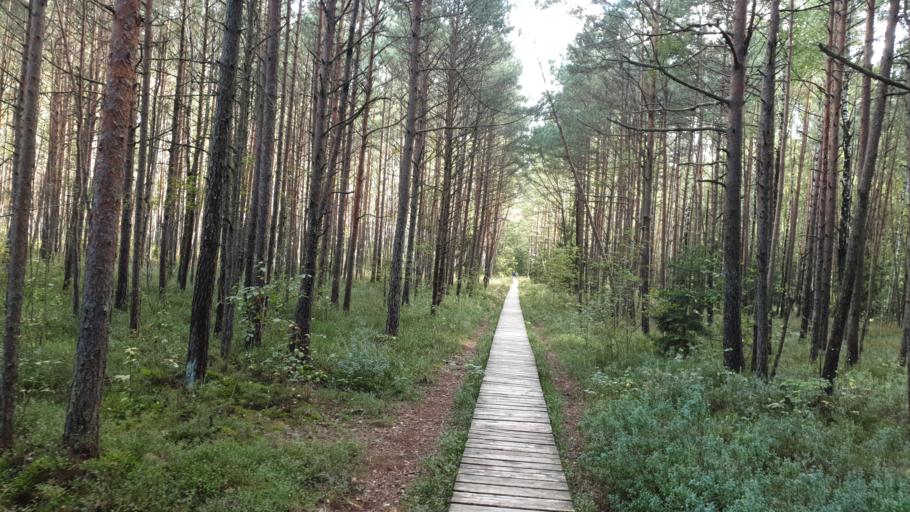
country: LT
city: Trakai
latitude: 54.6412
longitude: 24.9685
